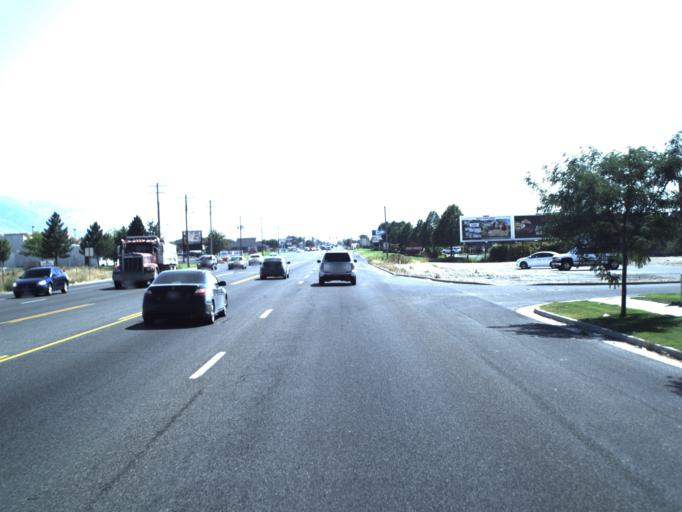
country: US
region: Utah
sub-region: Cache County
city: Hyde Park
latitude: 41.7764
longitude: -111.8341
